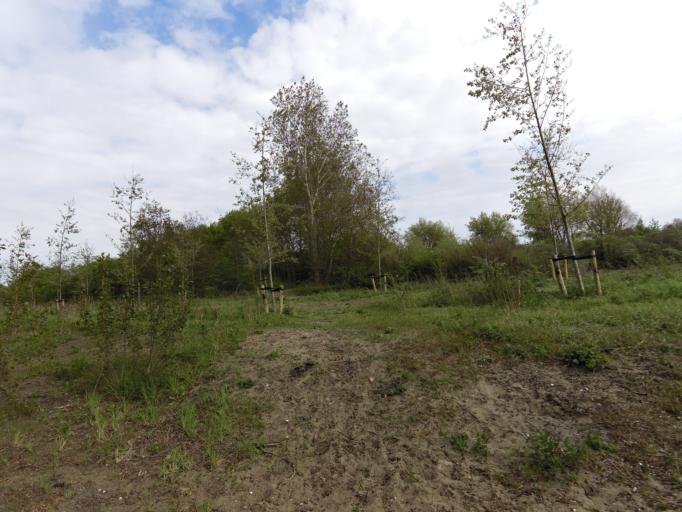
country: NL
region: South Holland
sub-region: Gemeente Goeree-Overflakkee
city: Ouddorp
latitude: 51.7824
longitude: 3.8886
